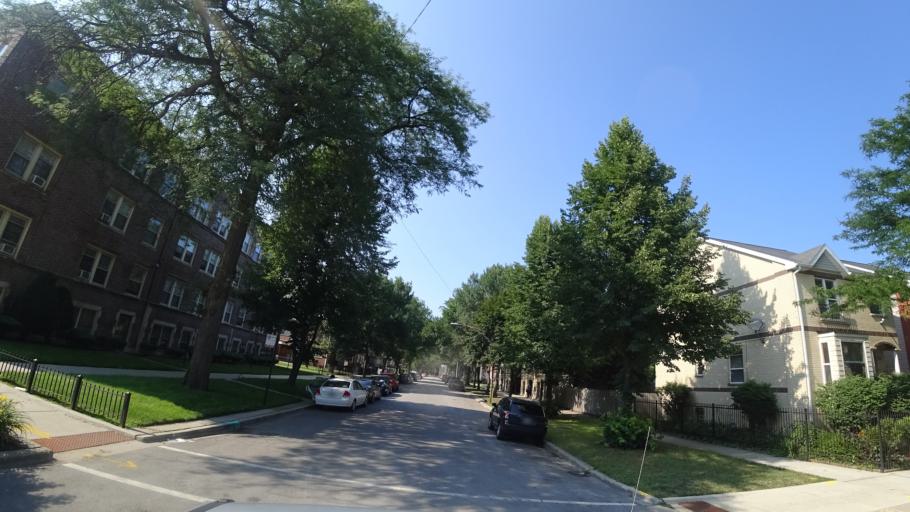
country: US
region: Illinois
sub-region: Cook County
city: Chicago
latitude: 41.7679
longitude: -87.5844
